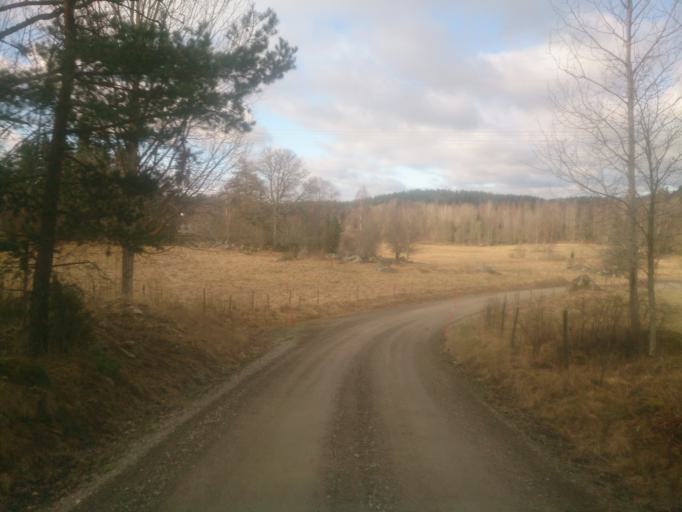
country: SE
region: OEstergoetland
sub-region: Atvidabergs Kommun
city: Atvidaberg
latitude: 58.2218
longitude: 16.1701
